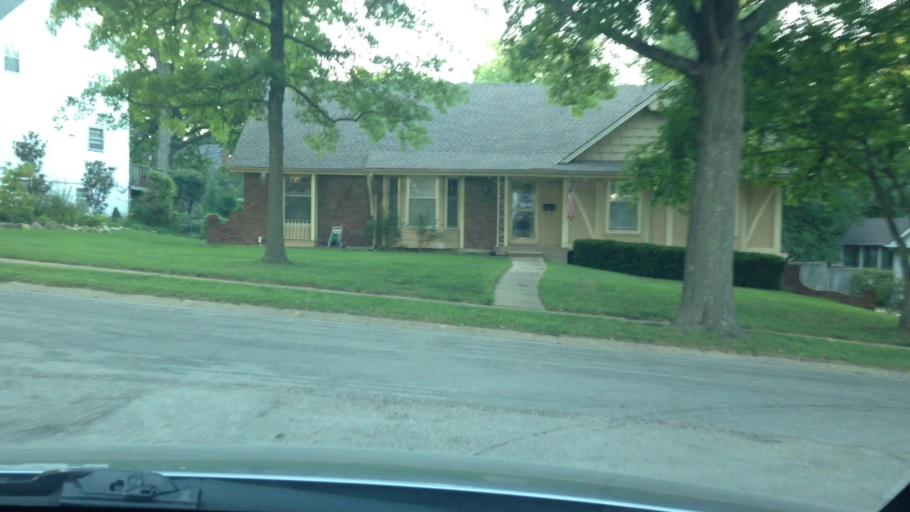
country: US
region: Kansas
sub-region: Johnson County
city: Leawood
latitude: 38.9142
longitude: -94.5914
